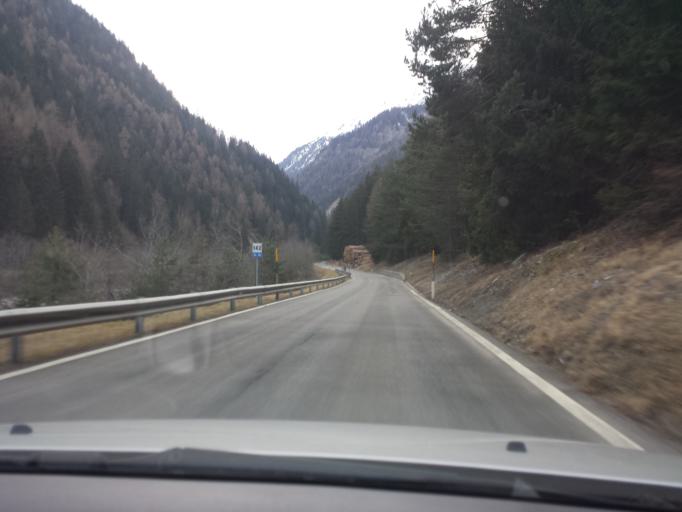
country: IT
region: Trentino-Alto Adige
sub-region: Bolzano
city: Stelvio
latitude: 46.5733
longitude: 10.5345
